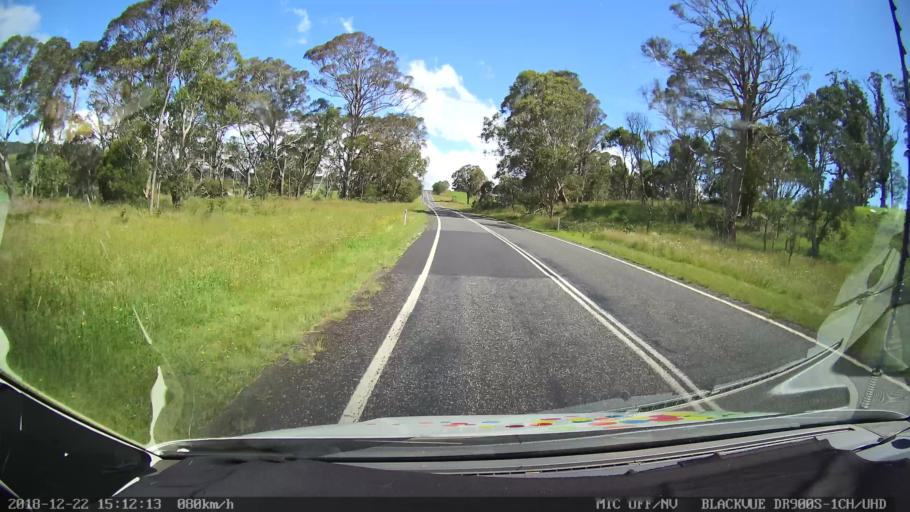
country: AU
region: New South Wales
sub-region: Bellingen
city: Dorrigo
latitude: -30.3530
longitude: 152.3968
